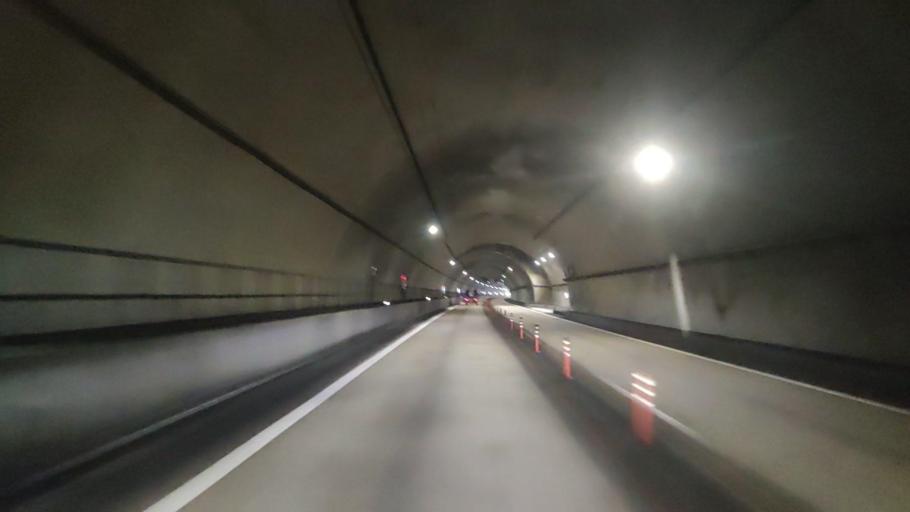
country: JP
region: Wakayama
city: Tanabe
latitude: 33.5498
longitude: 135.5159
